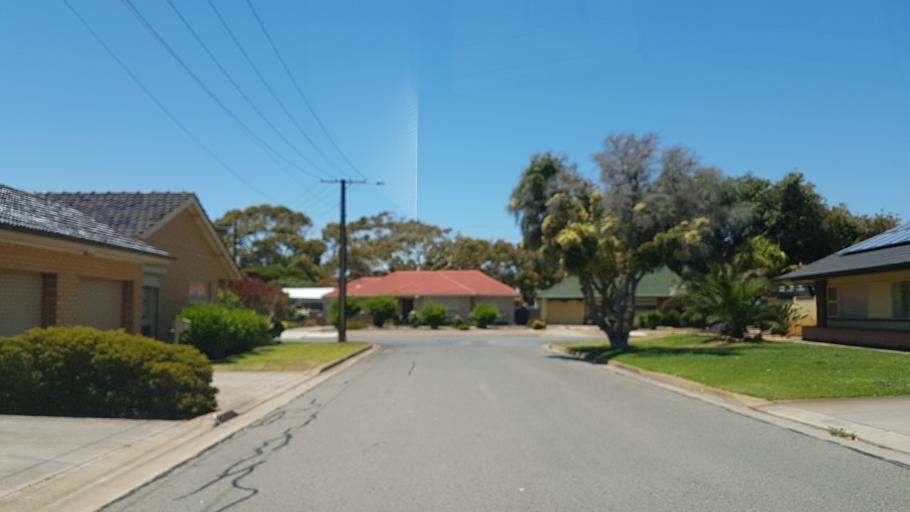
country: AU
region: South Australia
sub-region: Charles Sturt
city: West Lakes Shore
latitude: -34.8591
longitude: 138.4838
